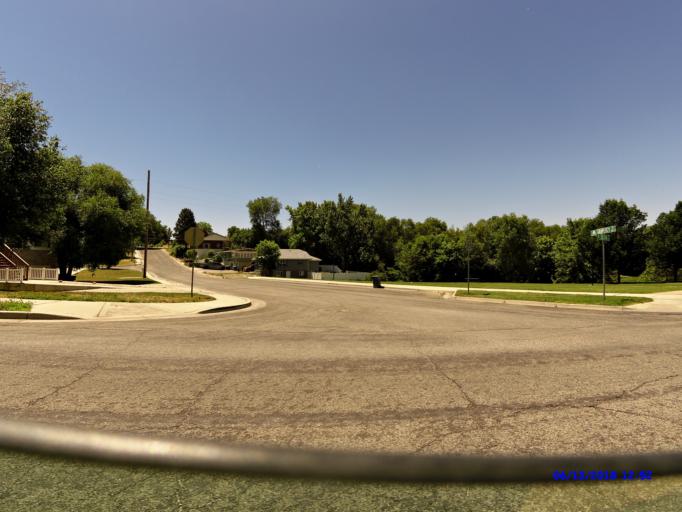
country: US
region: Utah
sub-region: Weber County
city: South Ogden
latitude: 41.2084
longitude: -111.9583
